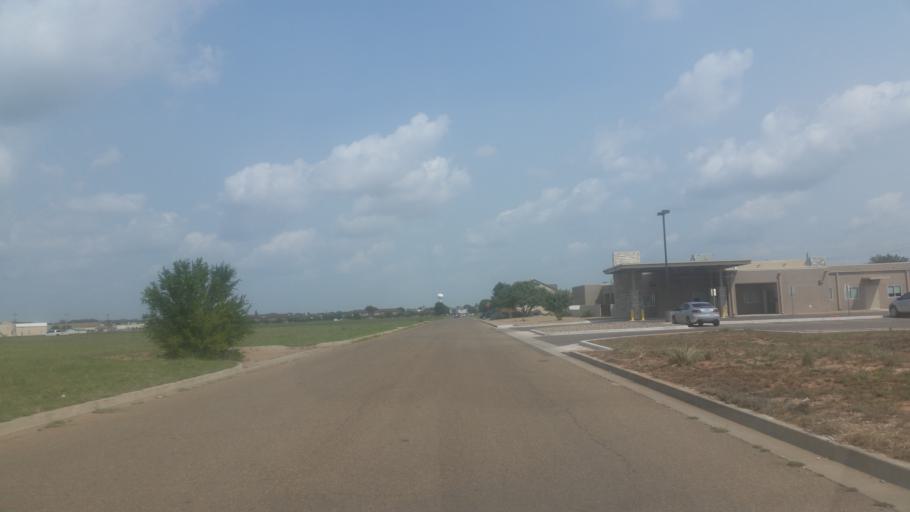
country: US
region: New Mexico
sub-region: Curry County
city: Clovis
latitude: 34.4310
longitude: -103.2094
